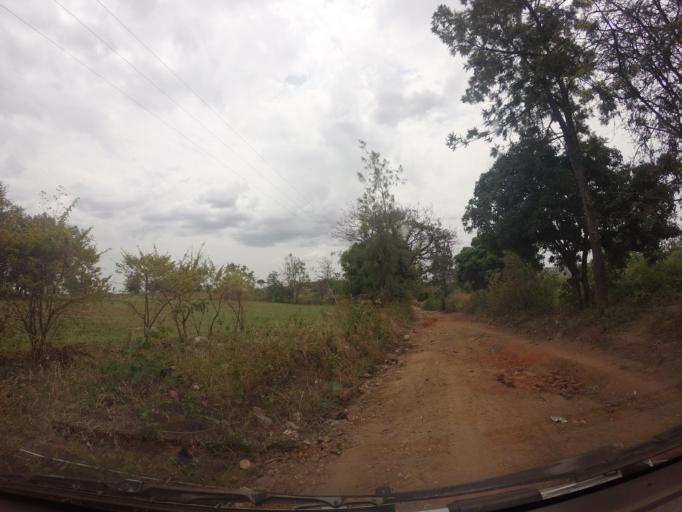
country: UG
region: Northern Region
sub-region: Arua District
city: Arua
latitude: 2.9425
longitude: 30.9397
